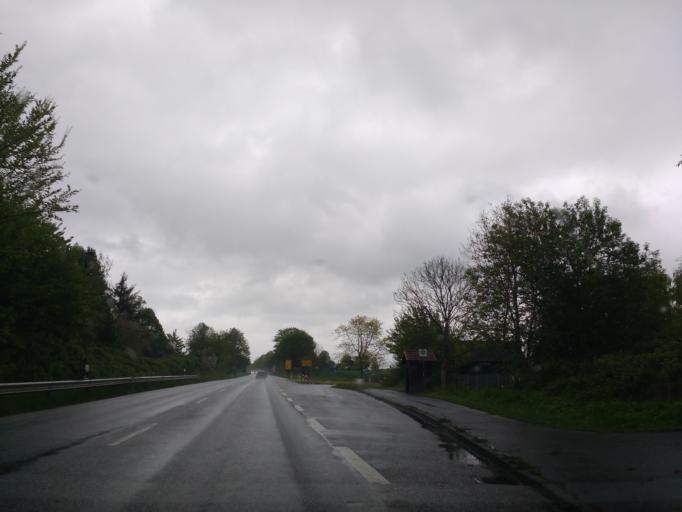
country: DE
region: Schleswig-Holstein
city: Loose
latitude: 54.5218
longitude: 9.8830
